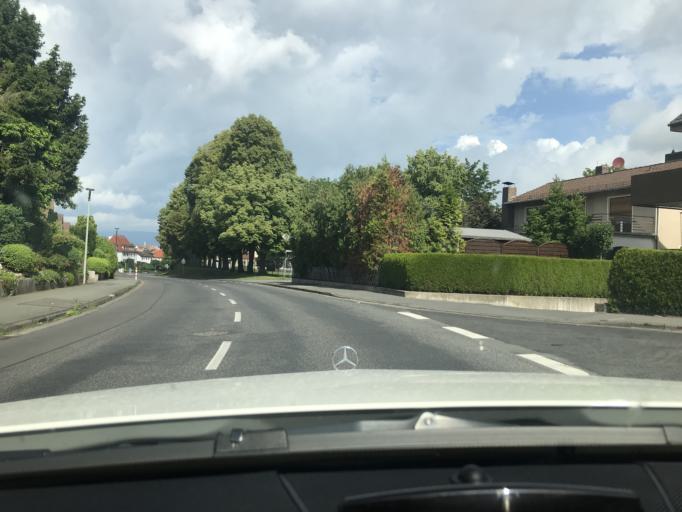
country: DE
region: Hesse
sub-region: Regierungsbezirk Kassel
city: Eschwege
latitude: 51.1827
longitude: 10.0700
